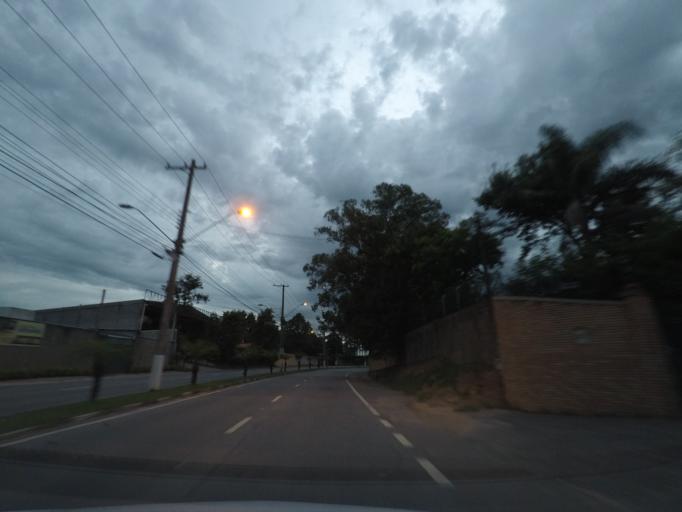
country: BR
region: Sao Paulo
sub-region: Vinhedo
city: Vinhedo
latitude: -23.0360
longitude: -46.9947
